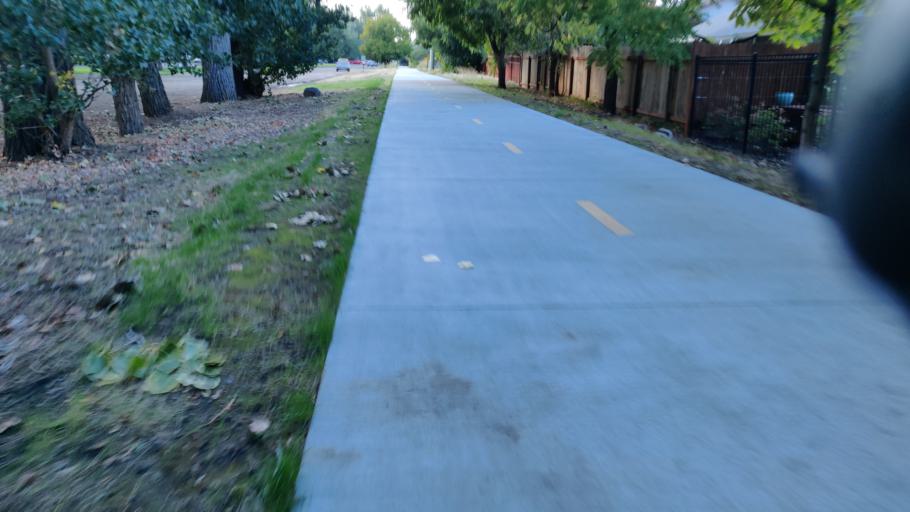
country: US
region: Idaho
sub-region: Ada County
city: Boise
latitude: 43.6031
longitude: -116.1822
